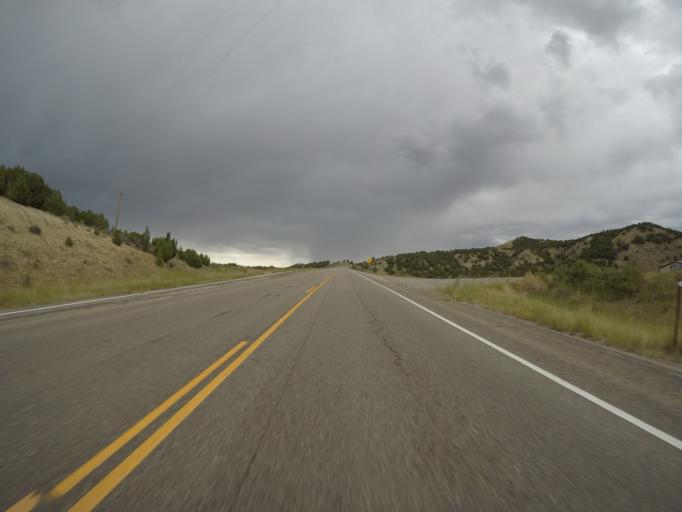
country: US
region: Colorado
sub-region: Rio Blanco County
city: Rangely
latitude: 40.3508
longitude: -108.4533
